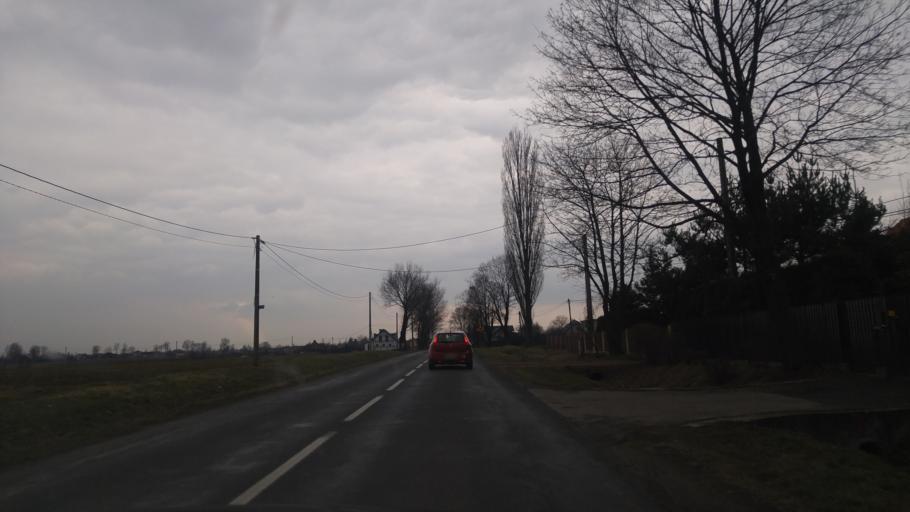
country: PL
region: Silesian Voivodeship
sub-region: Powiat cieszynski
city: Chybie
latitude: 49.9473
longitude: 18.8381
